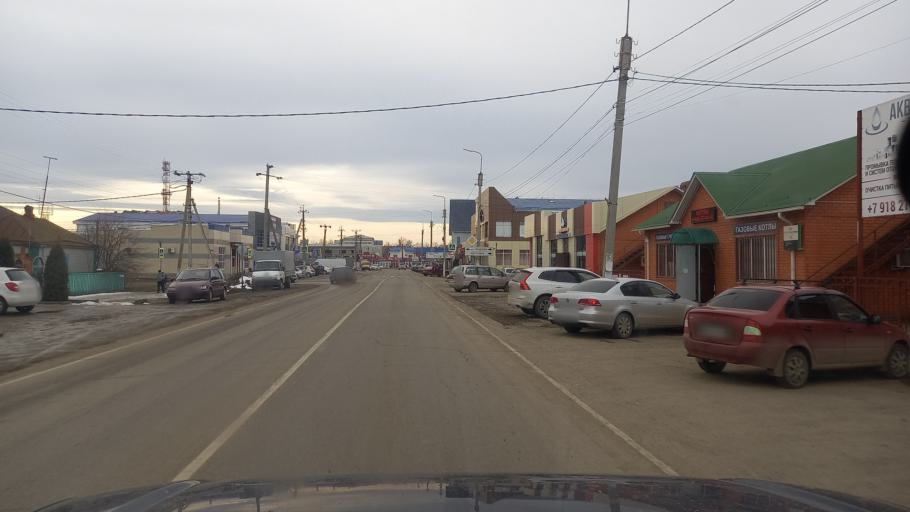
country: RU
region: Krasnodarskiy
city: Belorechensk
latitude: 44.7665
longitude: 39.8744
